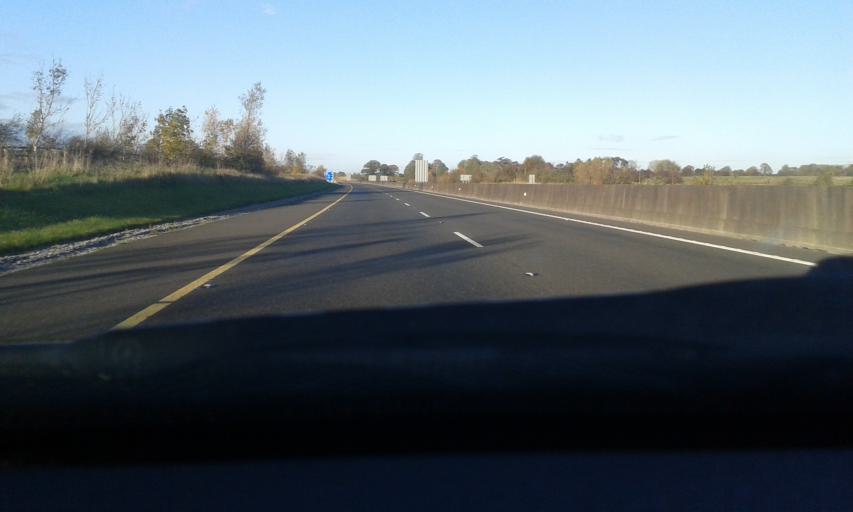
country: IE
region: Leinster
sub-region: Laois
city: Rathdowney
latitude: 52.7368
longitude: -7.5790
